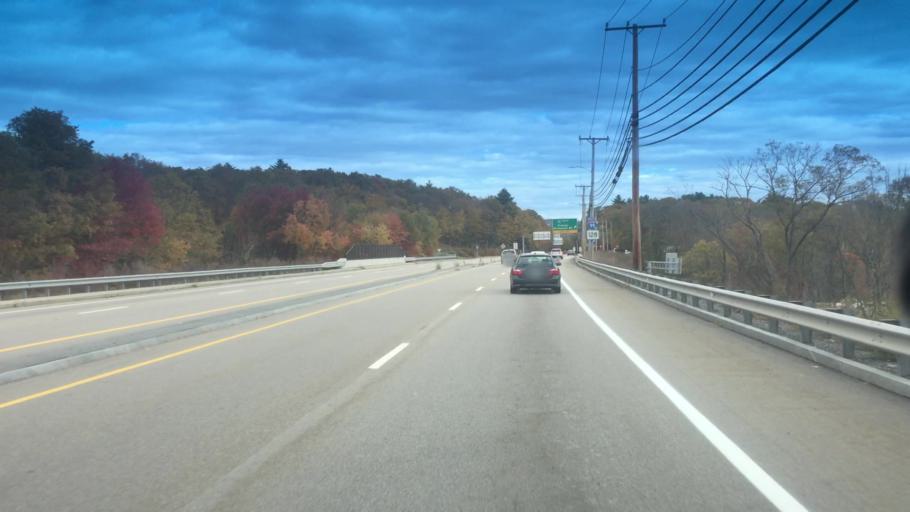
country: US
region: Massachusetts
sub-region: Norfolk County
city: Westwood
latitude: 42.2440
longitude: -71.2032
